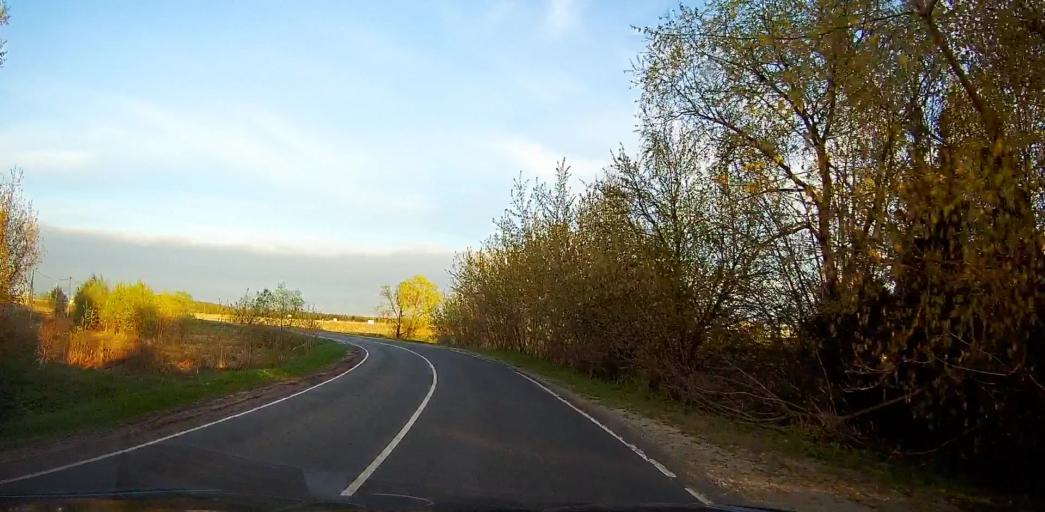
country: RU
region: Moskovskaya
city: Peski
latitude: 55.2106
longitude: 38.6748
